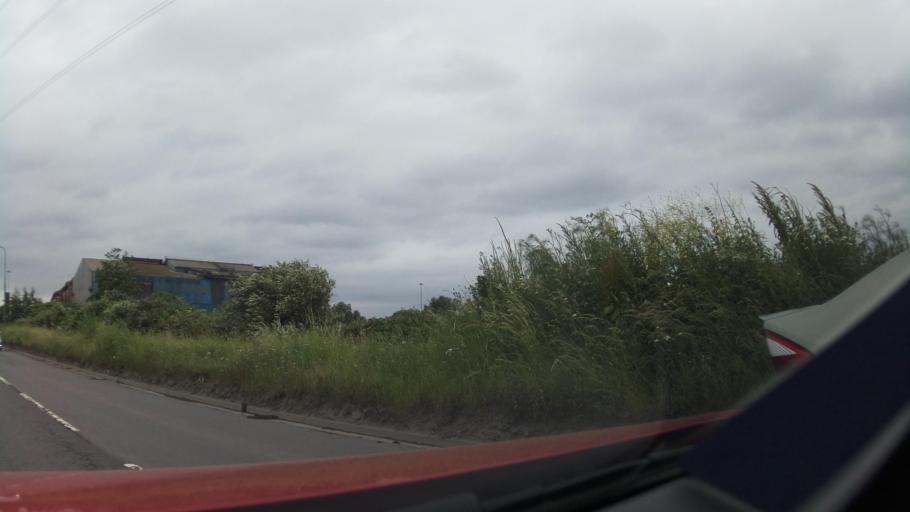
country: GB
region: Wales
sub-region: Cardiff
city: Cardiff
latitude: 51.4836
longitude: -3.1284
